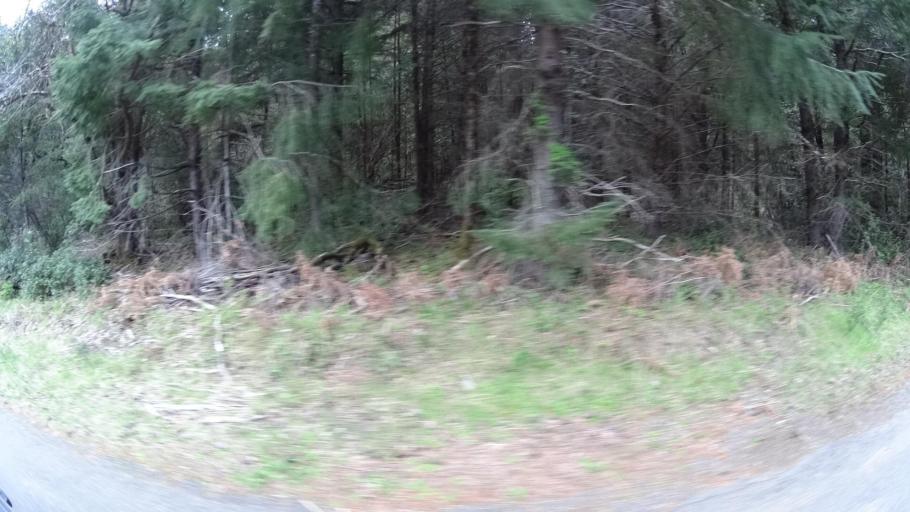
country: US
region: California
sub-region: Humboldt County
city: Redway
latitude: 40.0089
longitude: -123.9297
